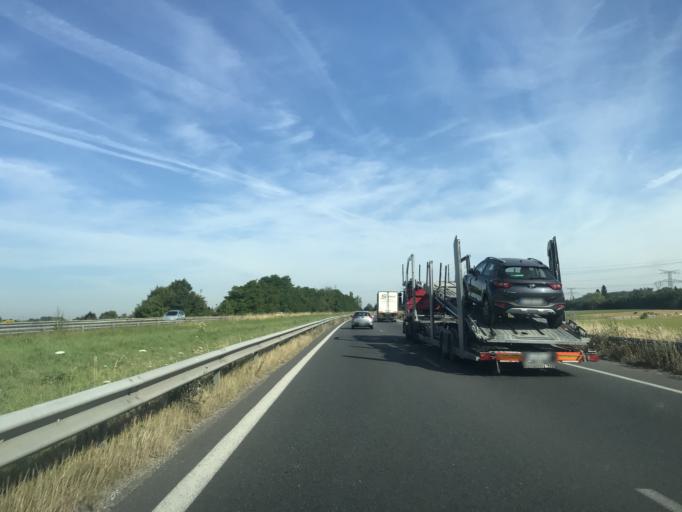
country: FR
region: Haute-Normandie
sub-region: Departement de la Seine-Maritime
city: La Vaupaliere
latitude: 49.4841
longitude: 1.0048
